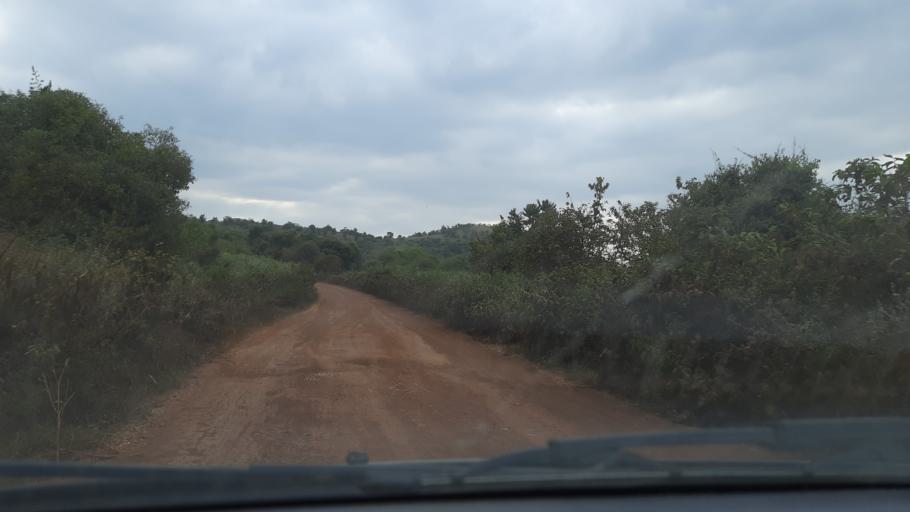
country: TZ
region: Kilimanjaro
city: Moshi
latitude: -2.8580
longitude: 37.2569
